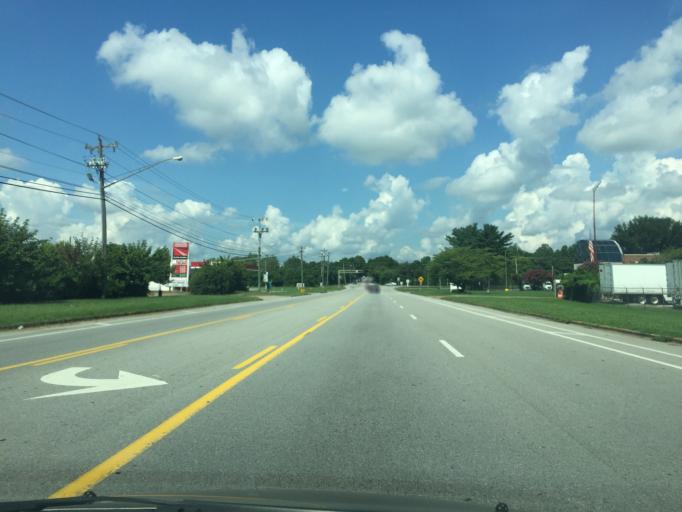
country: US
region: Tennessee
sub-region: Hamilton County
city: East Chattanooga
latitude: 35.0550
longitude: -85.1972
